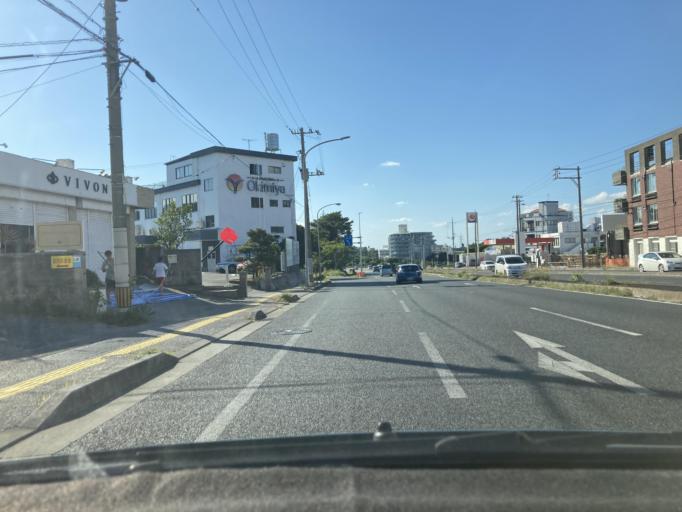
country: JP
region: Okinawa
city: Ginowan
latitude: 26.2554
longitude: 127.7313
